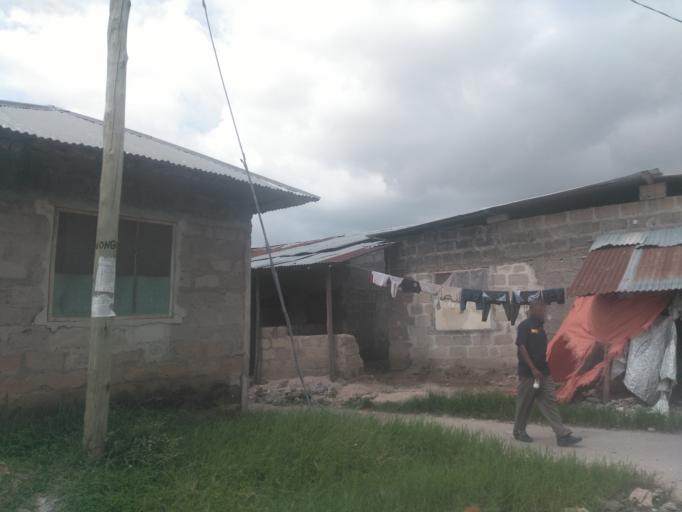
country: TZ
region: Zanzibar Urban/West
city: Zanzibar
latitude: -6.1782
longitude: 39.2396
